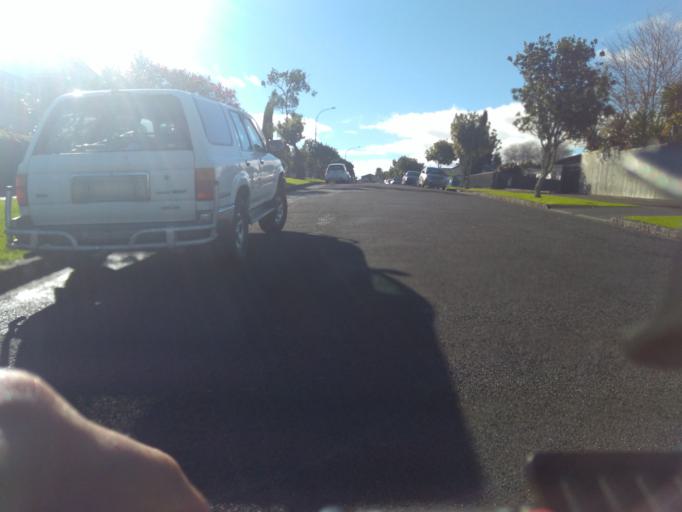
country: NZ
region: Auckland
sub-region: Auckland
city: Rosebank
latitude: -36.8702
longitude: 174.7077
